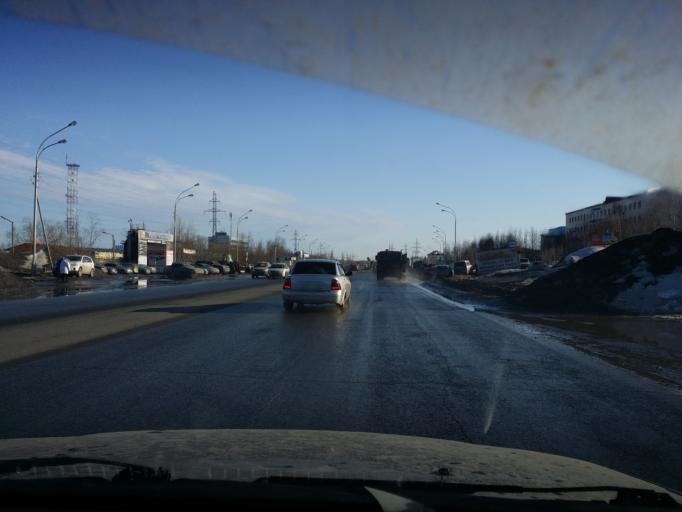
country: RU
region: Khanty-Mansiyskiy Avtonomnyy Okrug
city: Nizhnevartovsk
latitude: 60.9425
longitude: 76.5300
